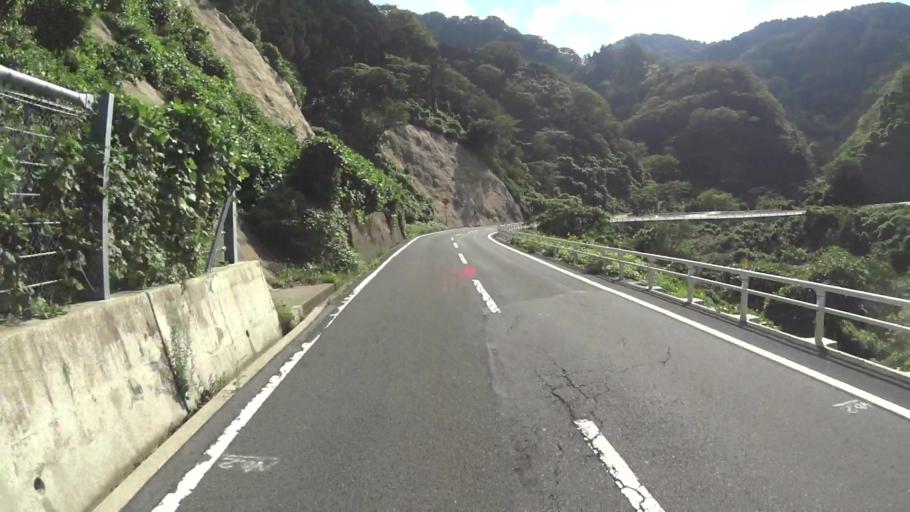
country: JP
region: Kyoto
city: Miyazu
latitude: 35.7635
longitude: 135.2370
